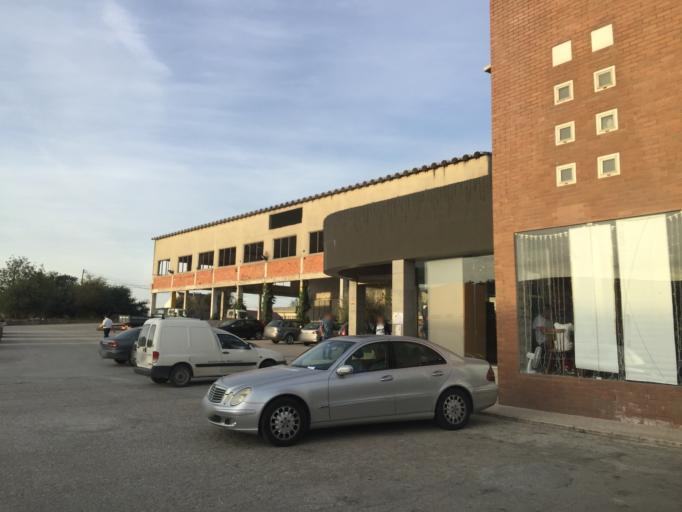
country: PT
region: Leiria
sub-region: Alcobaca
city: Benedita
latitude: 39.4339
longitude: -8.9569
